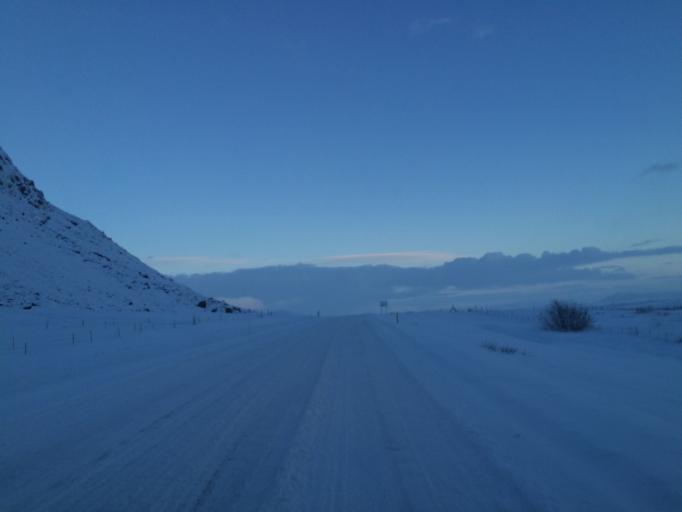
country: IS
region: South
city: Selfoss
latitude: 63.9600
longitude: -21.0074
